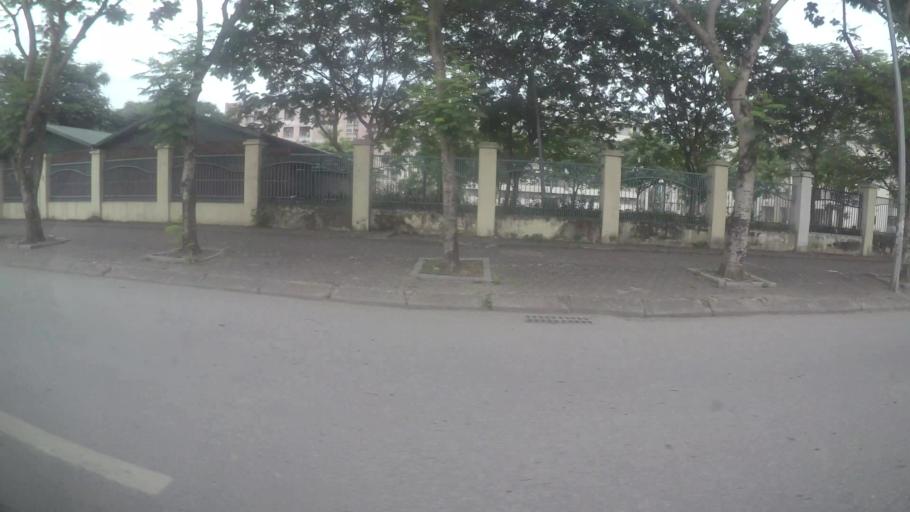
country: VN
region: Ha Noi
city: Cau Dien
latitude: 21.0248
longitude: 105.7641
